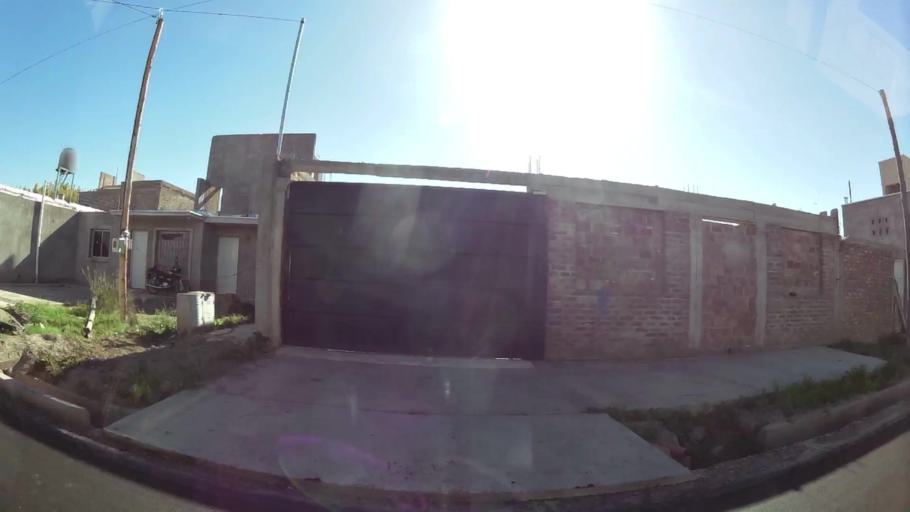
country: AR
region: Mendoza
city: Las Heras
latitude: -32.8490
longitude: -68.8294
